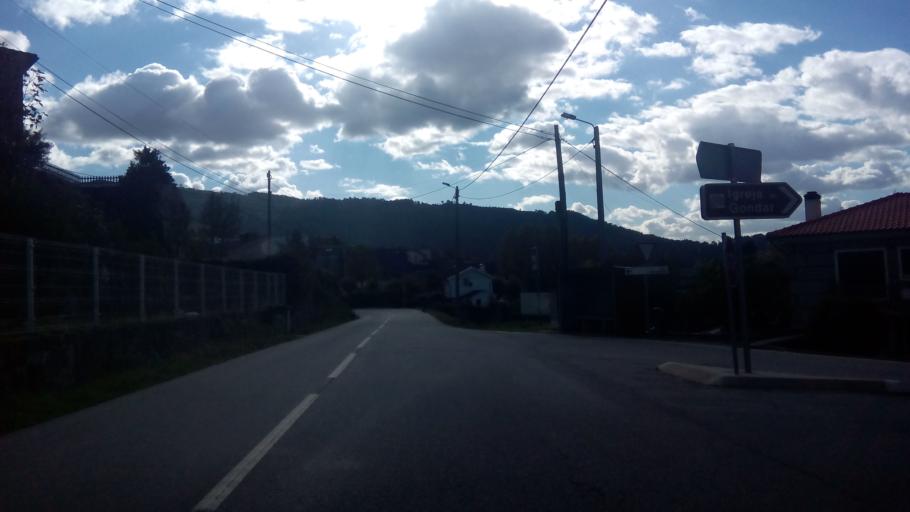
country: PT
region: Porto
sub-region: Amarante
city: Amarante
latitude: 41.2576
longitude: -8.0279
